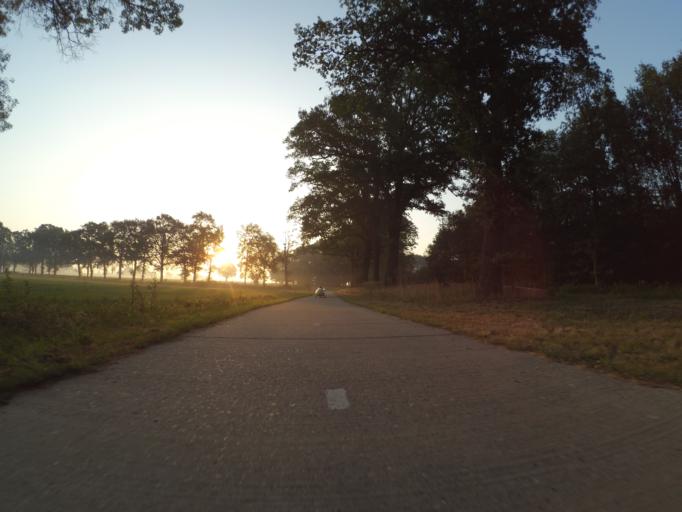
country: NL
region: Overijssel
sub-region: Gemeente Tubbergen
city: Tubbergen
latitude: 52.3996
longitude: 6.7643
